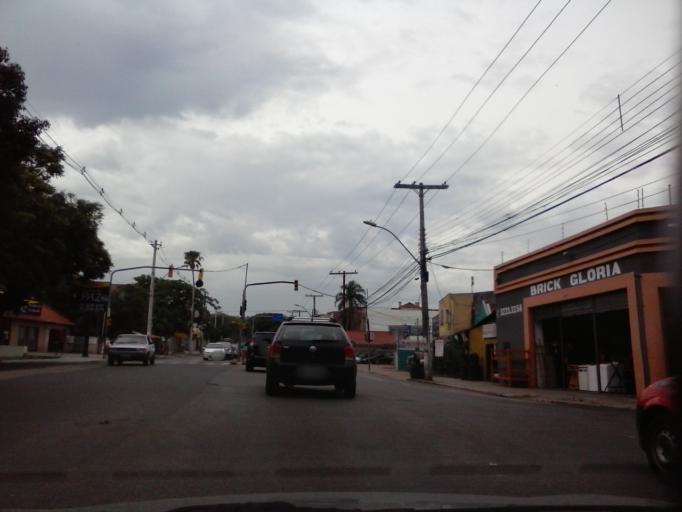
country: BR
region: Rio Grande do Sul
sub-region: Porto Alegre
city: Porto Alegre
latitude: -30.0687
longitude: -51.2052
